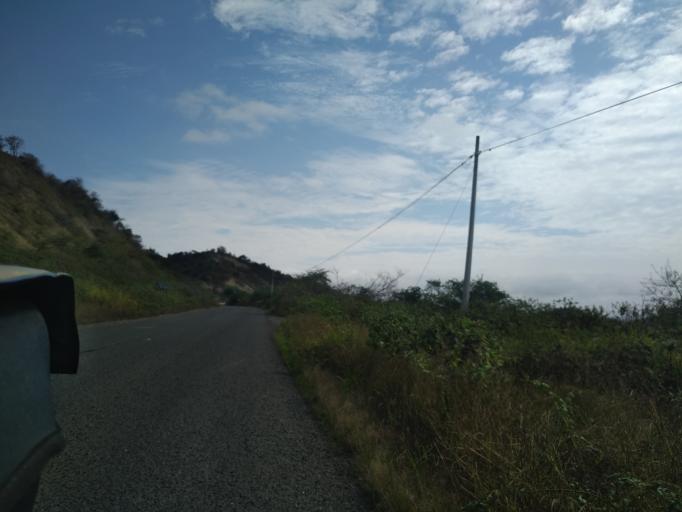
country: EC
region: Manabi
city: Jipijapa
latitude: -1.4351
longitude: -80.7541
